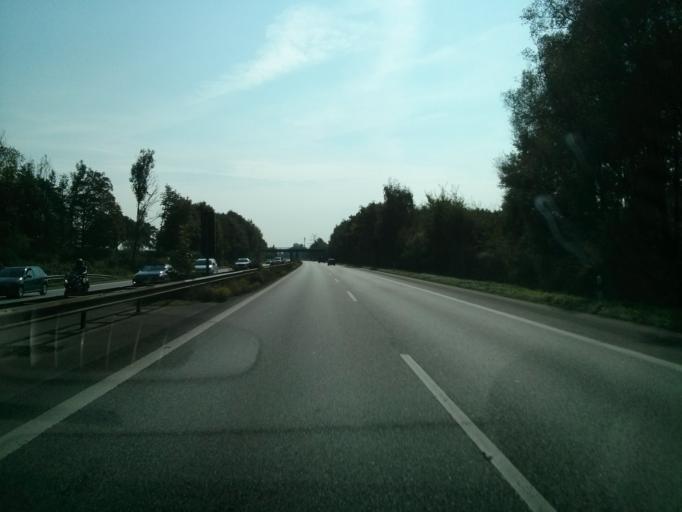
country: DE
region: Schleswig-Holstein
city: Kummerfeld
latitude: 53.6964
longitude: 9.7786
